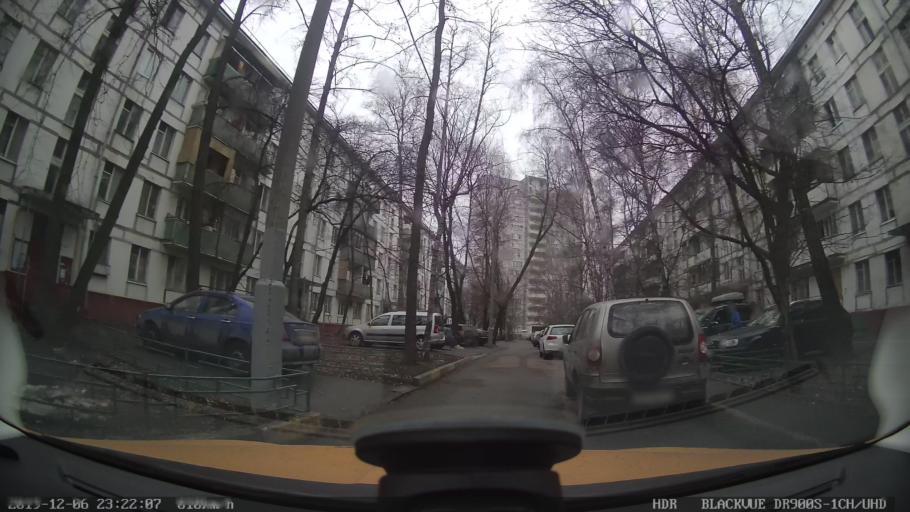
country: RU
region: Moscow
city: Zapadnoye Degunino
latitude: 55.8684
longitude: 37.5417
